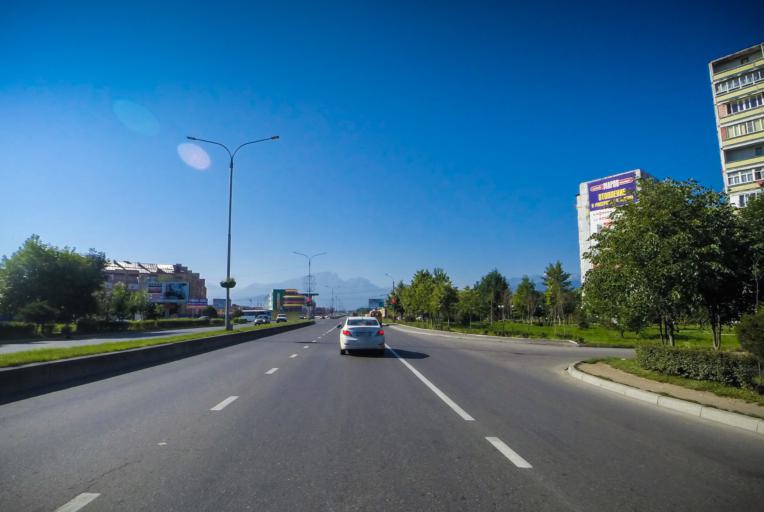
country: RU
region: North Ossetia
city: Vladikavkaz
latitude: 43.0372
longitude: 44.6409
